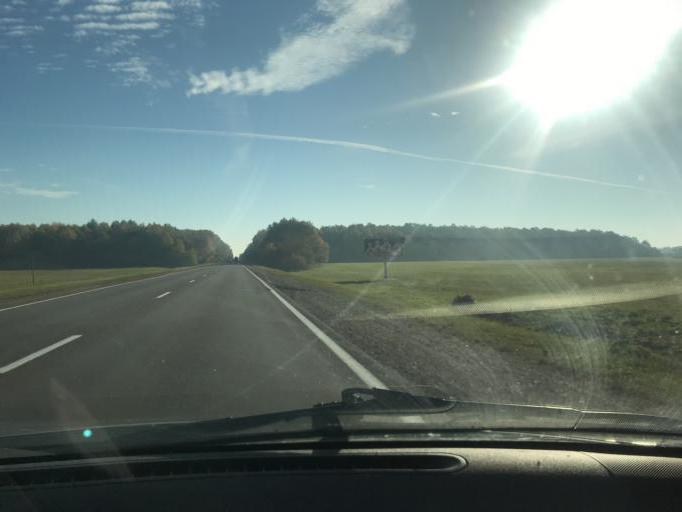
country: BY
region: Brest
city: Ivanava
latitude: 52.1540
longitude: 25.3492
